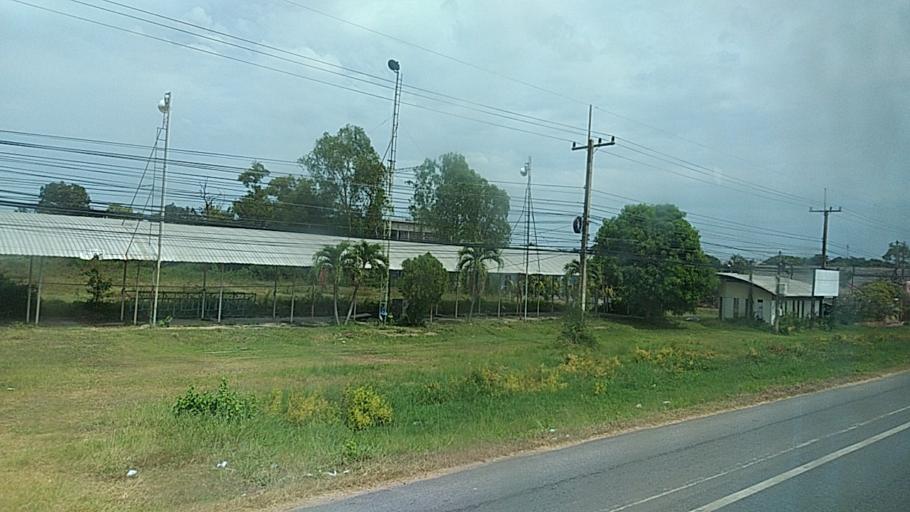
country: TH
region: Roi Et
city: Roi Et
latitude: 16.0722
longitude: 103.5975
